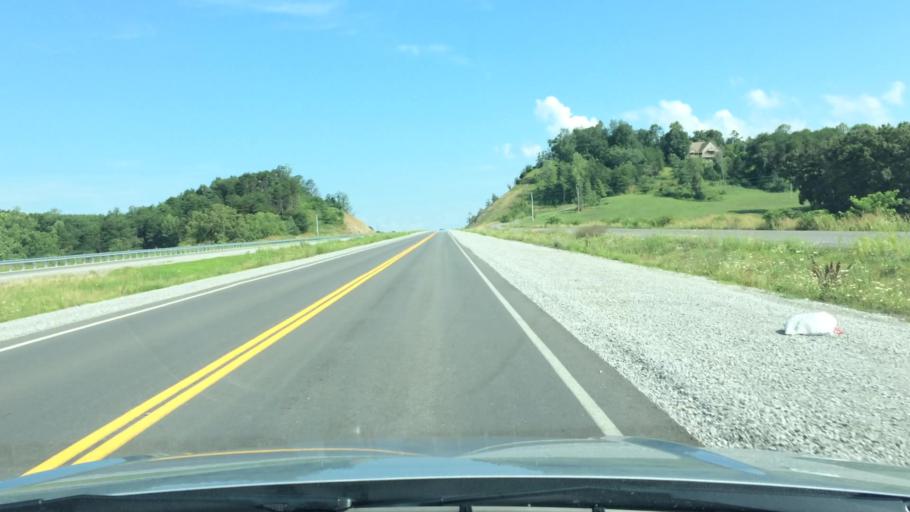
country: US
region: Tennessee
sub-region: Jefferson County
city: White Pine
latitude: 36.1321
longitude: -83.3367
